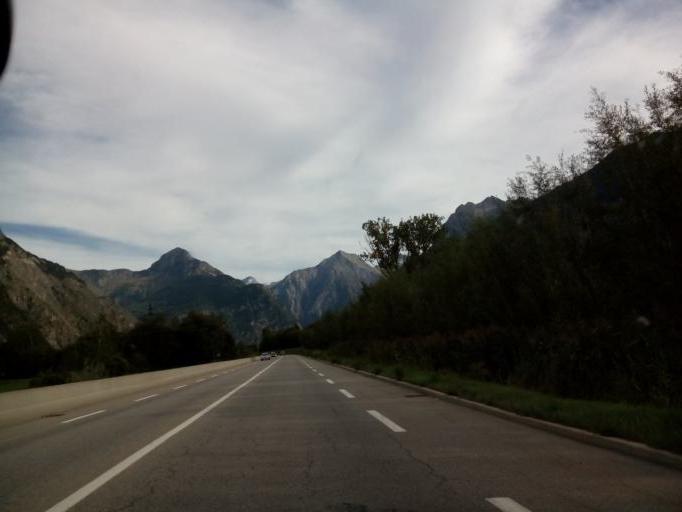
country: FR
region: Rhone-Alpes
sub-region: Departement de l'Isere
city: Huez
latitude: 45.0642
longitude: 6.0323
